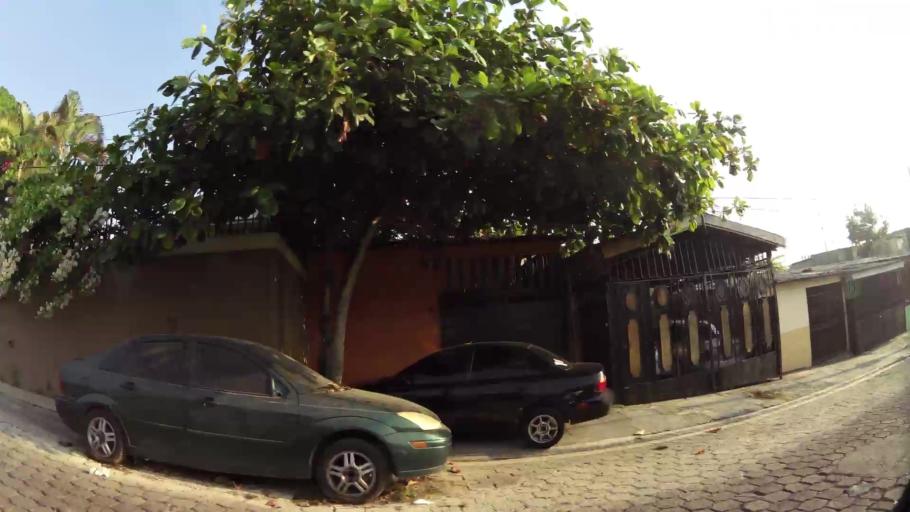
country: SV
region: San Salvador
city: San Salvador
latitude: 13.6809
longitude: -89.2045
